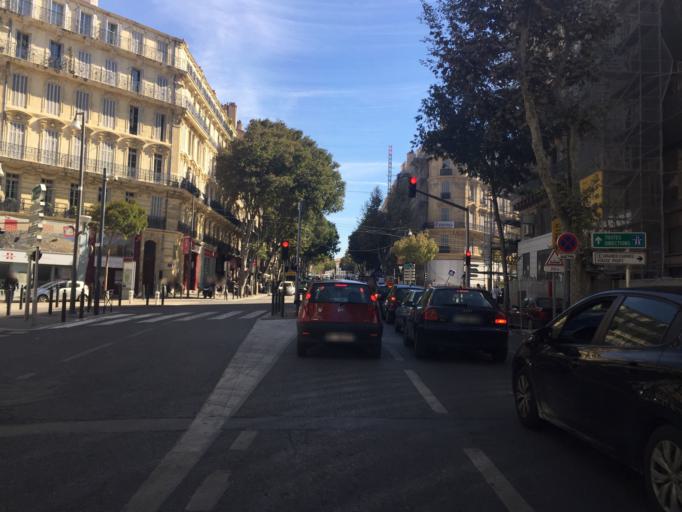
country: FR
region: Provence-Alpes-Cote d'Azur
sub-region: Departement des Bouches-du-Rhone
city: Marseille 02
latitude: 43.3027
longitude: 5.3684
